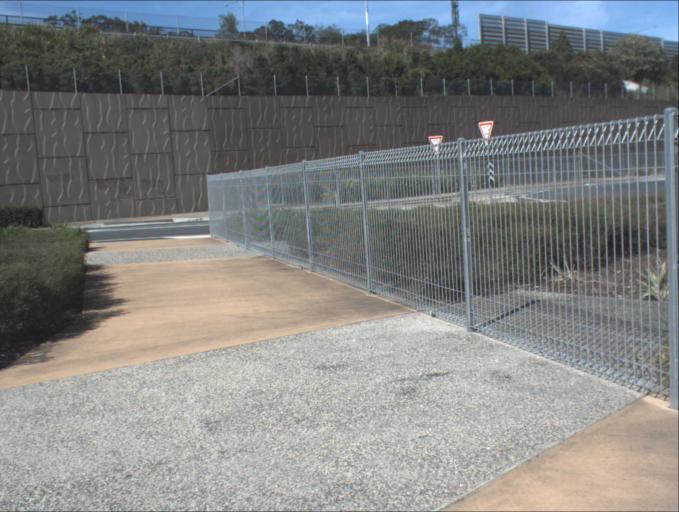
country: AU
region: Queensland
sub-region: Logan
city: Slacks Creek
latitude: -27.6457
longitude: 153.1467
